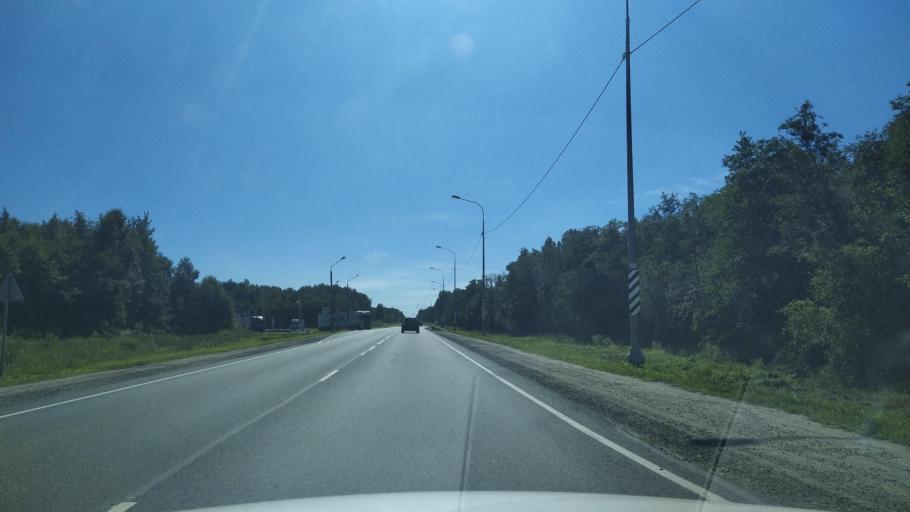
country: RU
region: Pskov
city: Pskov
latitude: 57.7843
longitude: 28.4072
